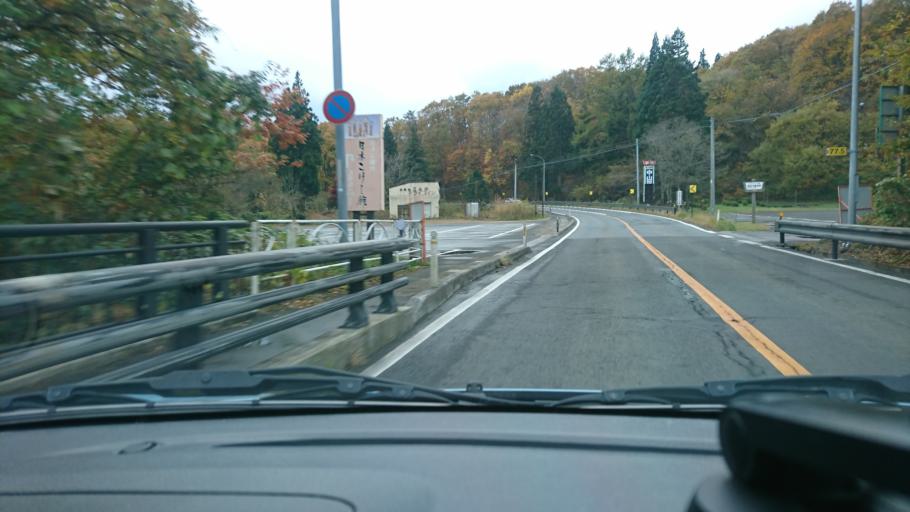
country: JP
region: Miyagi
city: Furukawa
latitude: 38.7354
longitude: 140.6882
